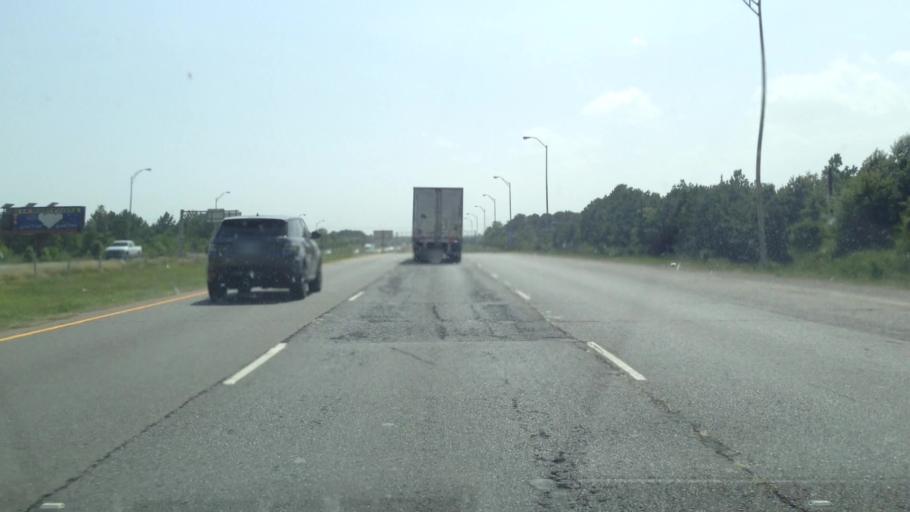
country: US
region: Louisiana
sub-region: Caddo Parish
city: Shreveport
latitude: 32.4603
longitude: -93.8320
